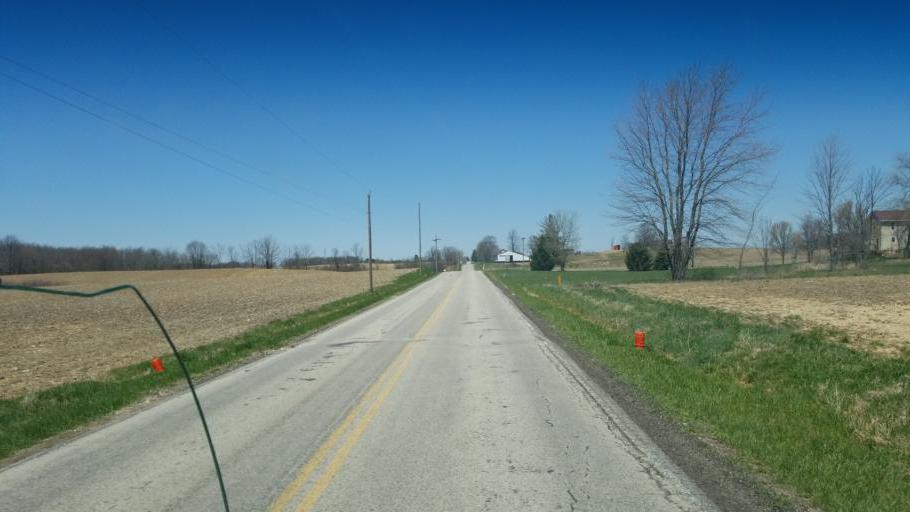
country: US
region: Ohio
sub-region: Richland County
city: Ontario
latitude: 40.8441
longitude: -82.5638
